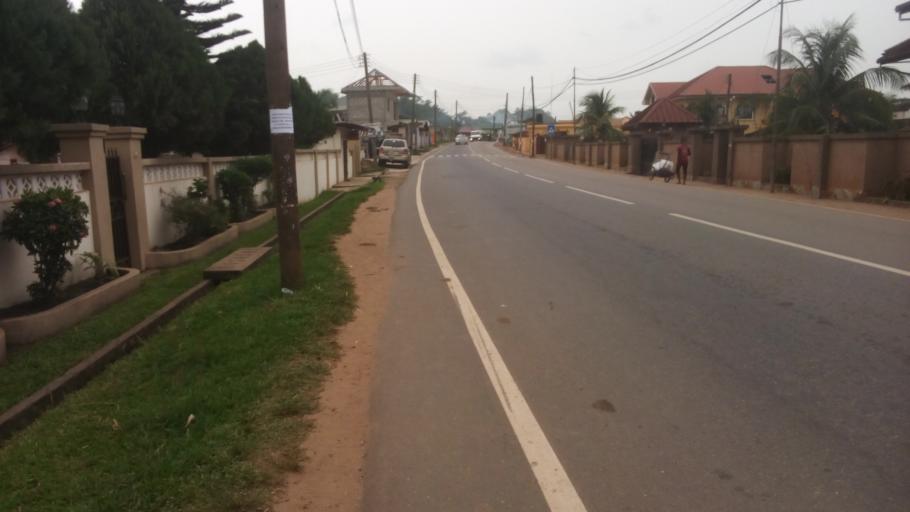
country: GH
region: Western
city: Tarkwa
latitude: 5.2844
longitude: -2.0009
